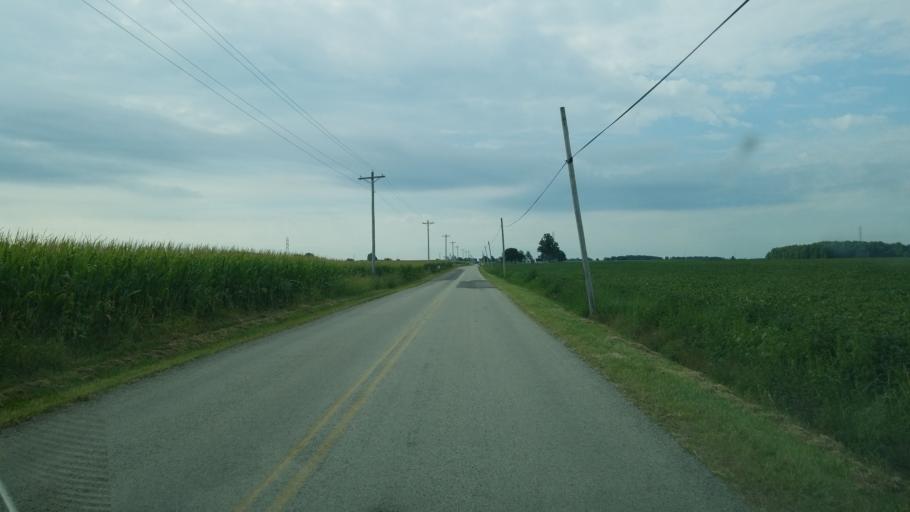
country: US
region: Ohio
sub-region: Richland County
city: Shelby
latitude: 40.8631
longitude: -82.7198
